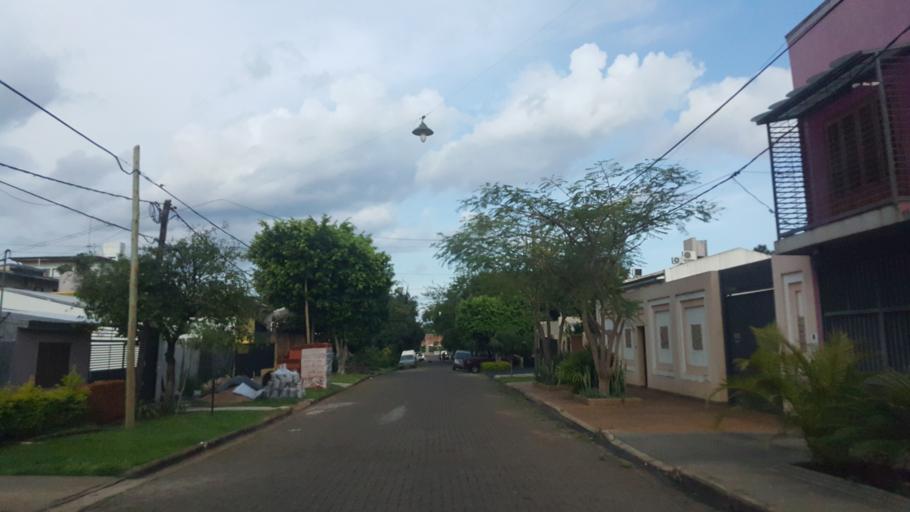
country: AR
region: Misiones
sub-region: Departamento de Capital
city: Posadas
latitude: -27.3803
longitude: -55.8939
